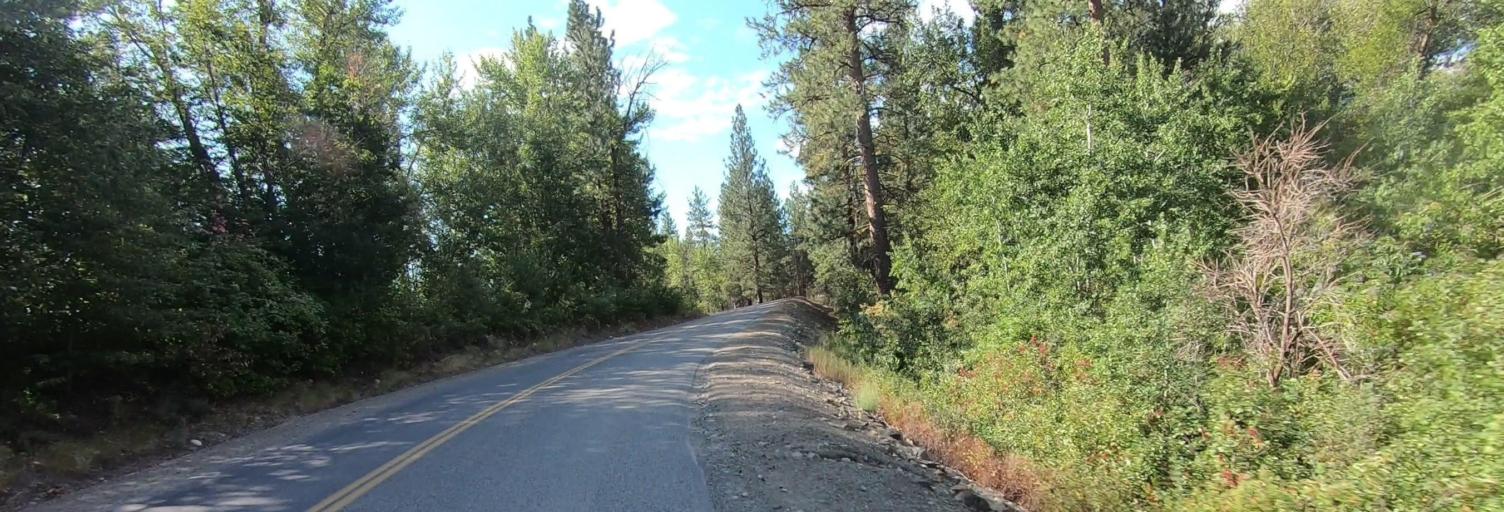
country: US
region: Washington
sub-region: Okanogan County
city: Brewster
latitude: 48.5298
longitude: -120.1780
